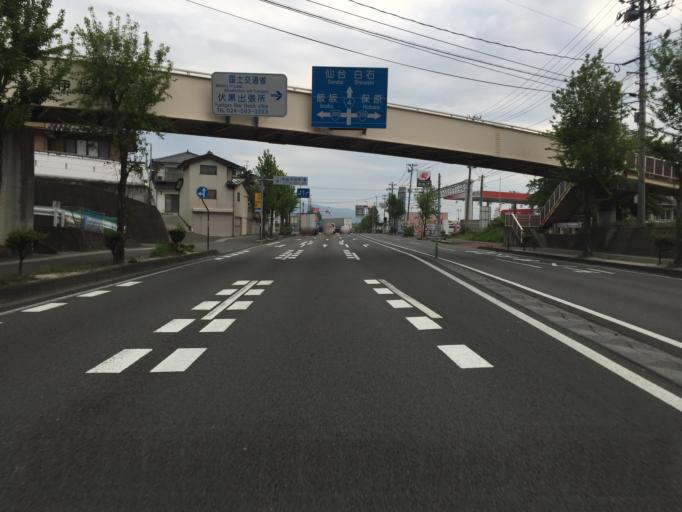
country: JP
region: Fukushima
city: Hobaramachi
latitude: 37.8190
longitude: 140.5040
